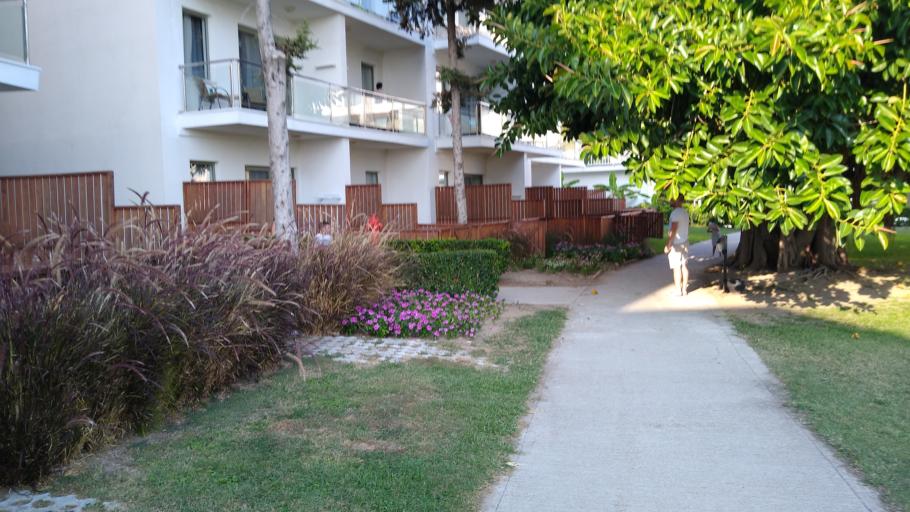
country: TR
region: Antalya
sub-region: Manavgat
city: Manavgat
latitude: 36.7517
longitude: 31.4528
